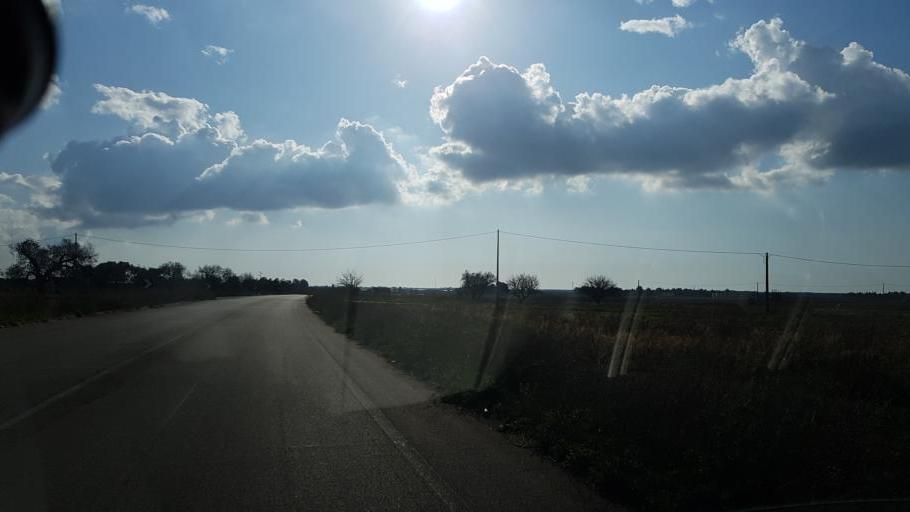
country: IT
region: Apulia
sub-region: Provincia di Lecce
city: Veglie
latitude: 40.3314
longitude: 17.9822
